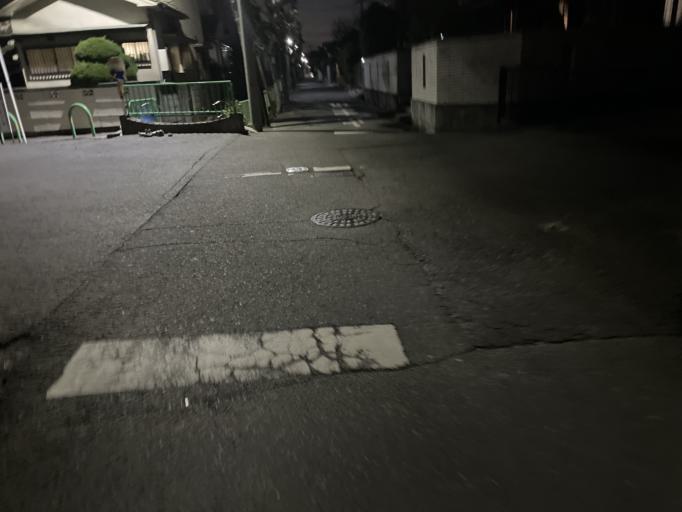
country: JP
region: Osaka
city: Ibaraki
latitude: 34.8080
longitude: 135.5797
